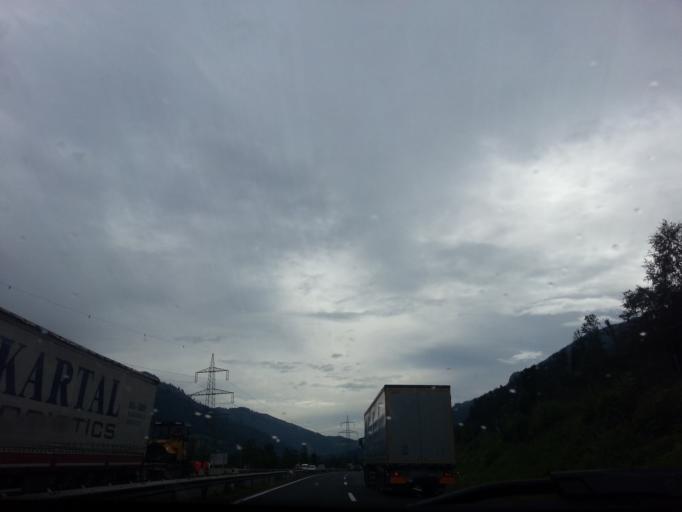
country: AT
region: Styria
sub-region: Politischer Bezirk Liezen
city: Treglwang
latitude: 47.4792
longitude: 14.5628
